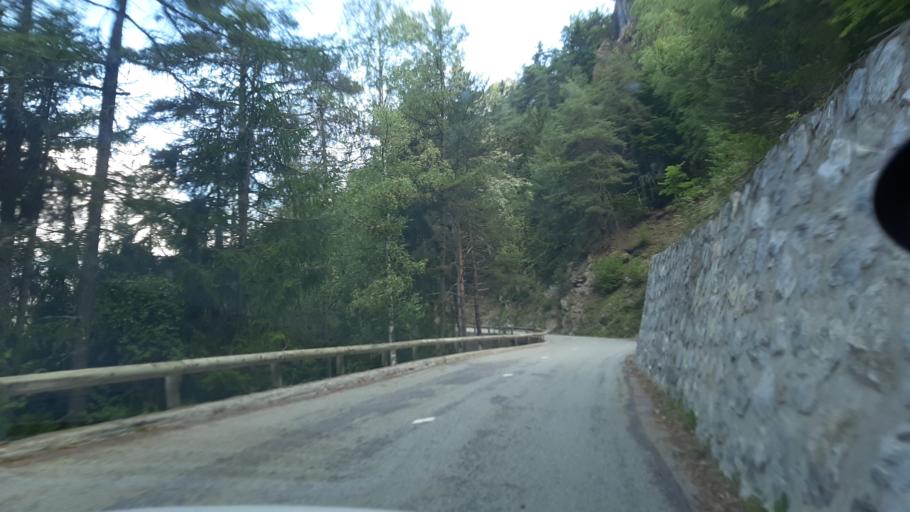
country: FR
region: Rhone-Alpes
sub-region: Departement de la Savoie
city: Aime
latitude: 45.5267
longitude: 6.6170
